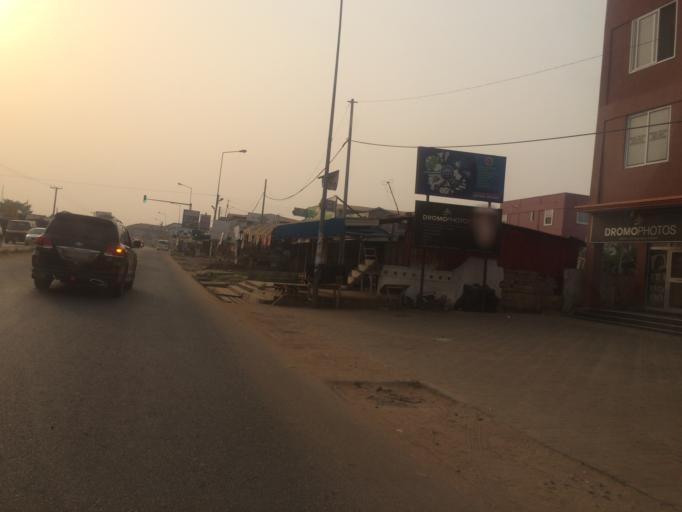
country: GH
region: Greater Accra
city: Nungua
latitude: 5.6383
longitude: -0.1054
